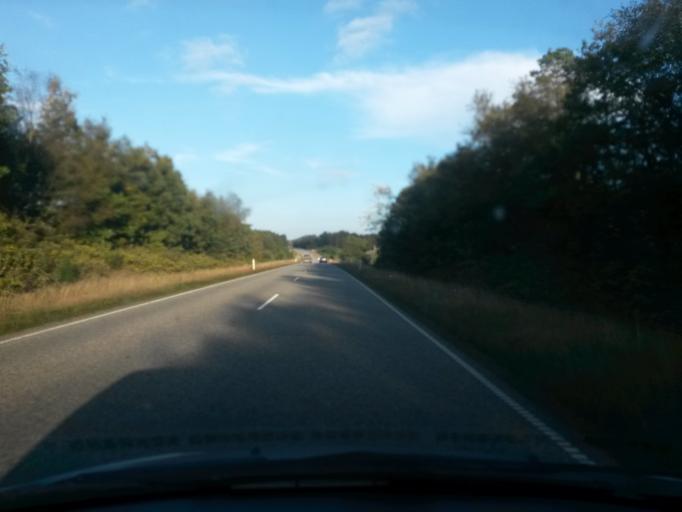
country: DK
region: Central Jutland
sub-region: Herning Kommune
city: Sunds
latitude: 56.3324
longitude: 9.0200
